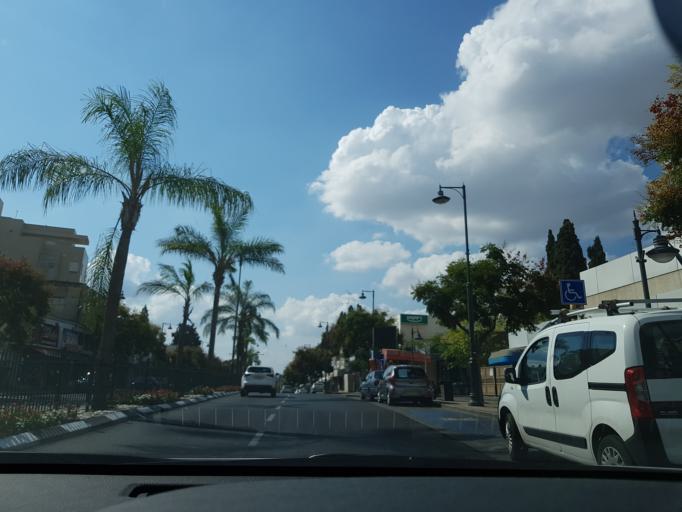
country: IL
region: Central District
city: Ness Ziona
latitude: 31.9281
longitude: 34.7982
